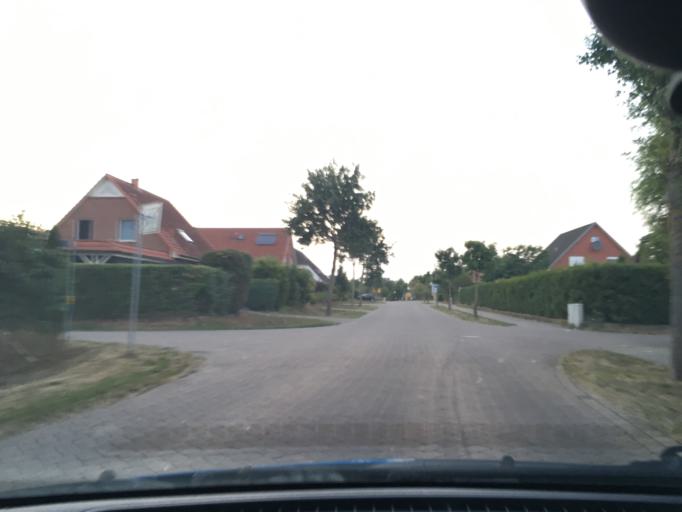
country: DE
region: Lower Saxony
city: Embsen
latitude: 53.1779
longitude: 10.3499
